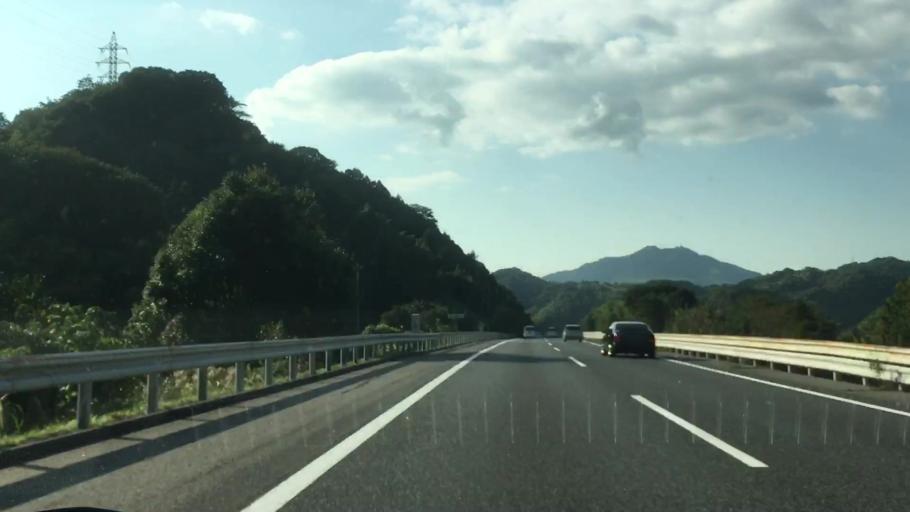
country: JP
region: Yamaguchi
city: Tokuyama
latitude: 34.0747
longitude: 131.8053
